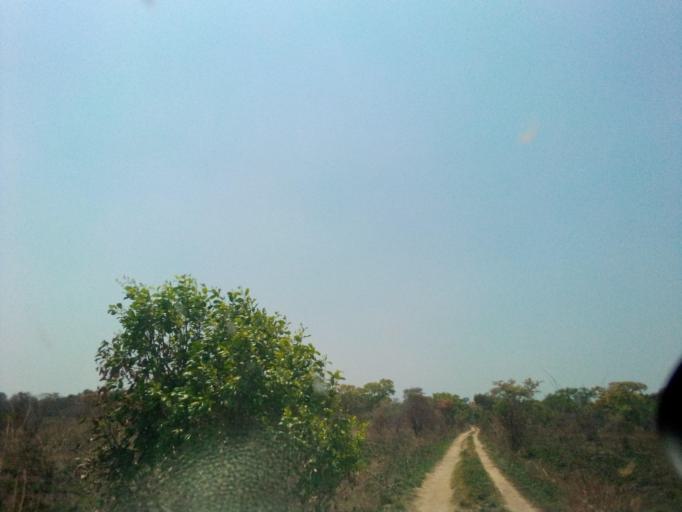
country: ZM
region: Copperbelt
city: Kataba
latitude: -12.2462
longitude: 30.3959
